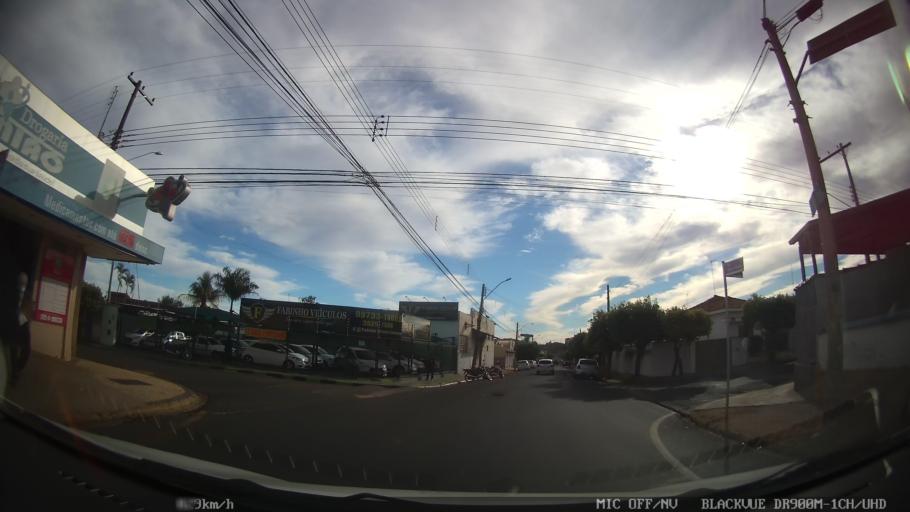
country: BR
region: Sao Paulo
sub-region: Catanduva
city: Catanduva
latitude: -21.1213
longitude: -48.9668
